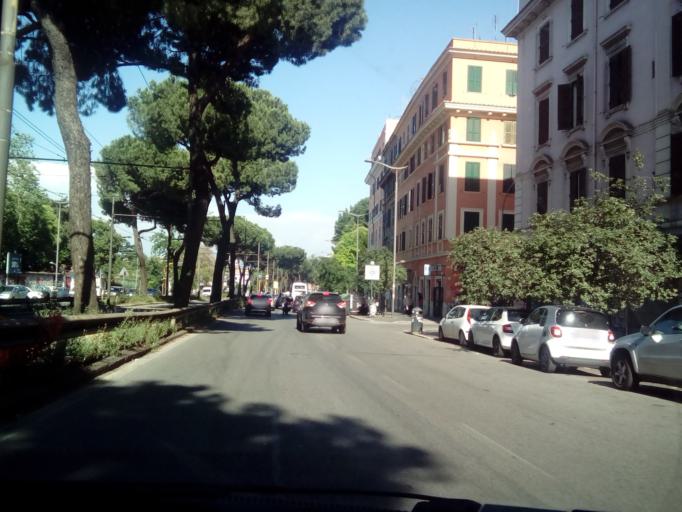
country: IT
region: Latium
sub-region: Citta metropolitana di Roma Capitale
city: Rome
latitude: 41.8923
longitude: 12.5347
